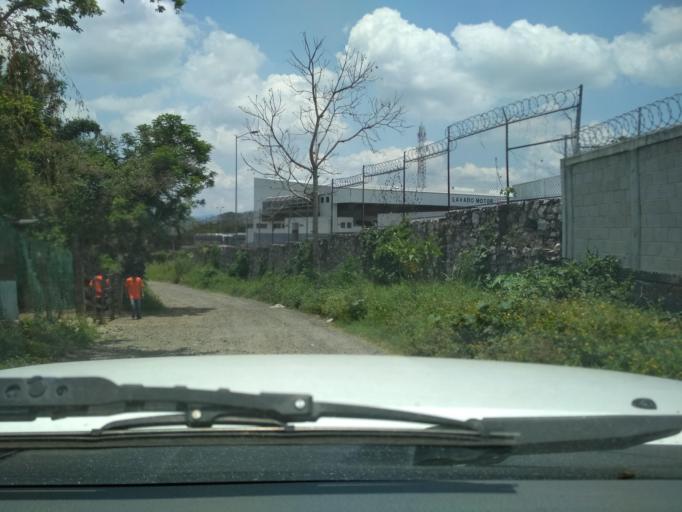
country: MX
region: Veracruz
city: Cordoba
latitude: 18.8844
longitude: -96.9183
